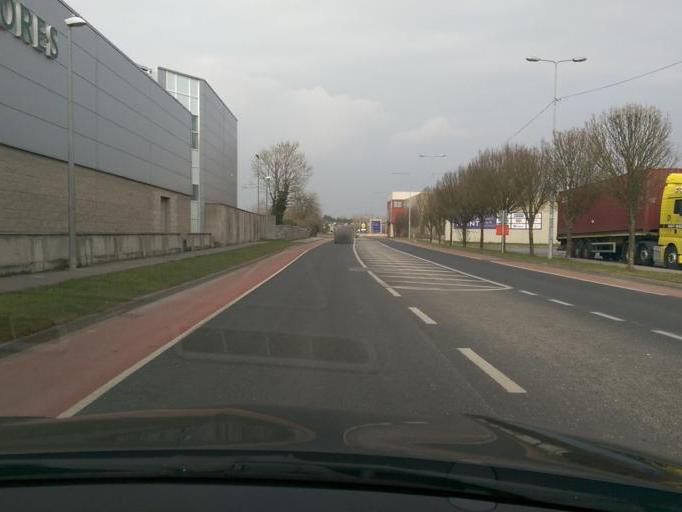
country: IE
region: Connaught
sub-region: Roscommon
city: Roscommon
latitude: 53.6320
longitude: -8.1839
